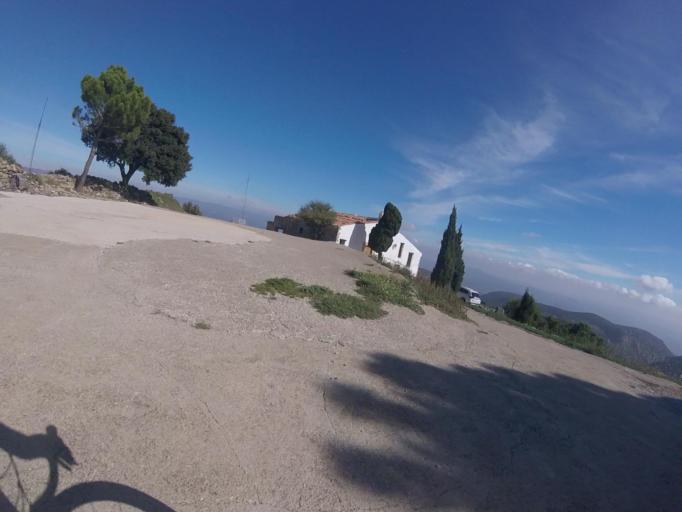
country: ES
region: Valencia
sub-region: Provincia de Castello
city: Sarratella
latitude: 40.3206
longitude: 0.0237
